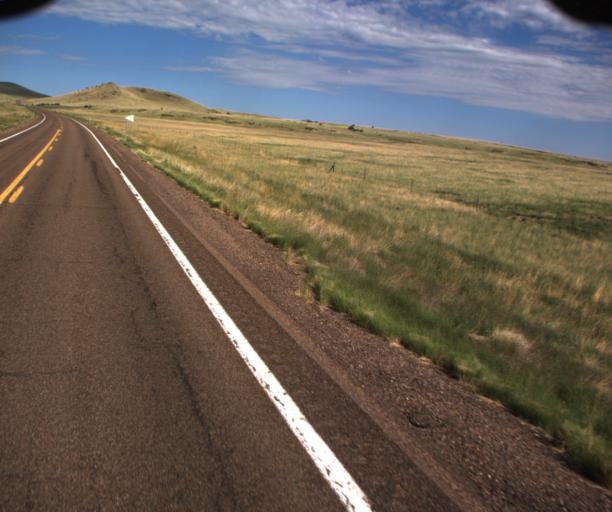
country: US
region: Arizona
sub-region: Apache County
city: Springerville
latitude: 34.2013
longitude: -109.4000
